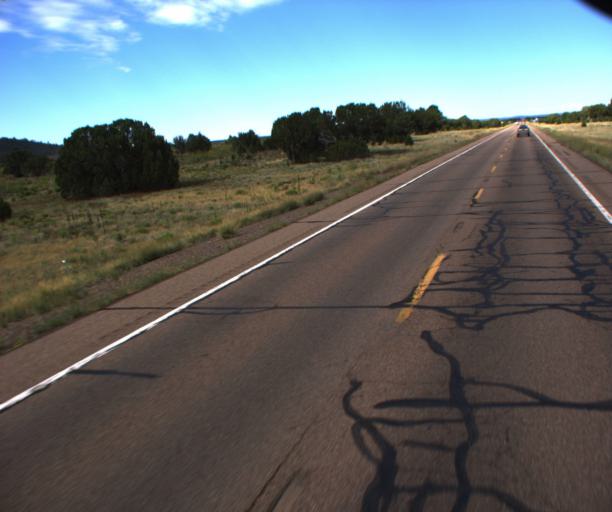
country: US
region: Arizona
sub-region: Navajo County
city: Show Low
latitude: 34.2702
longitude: -109.9271
